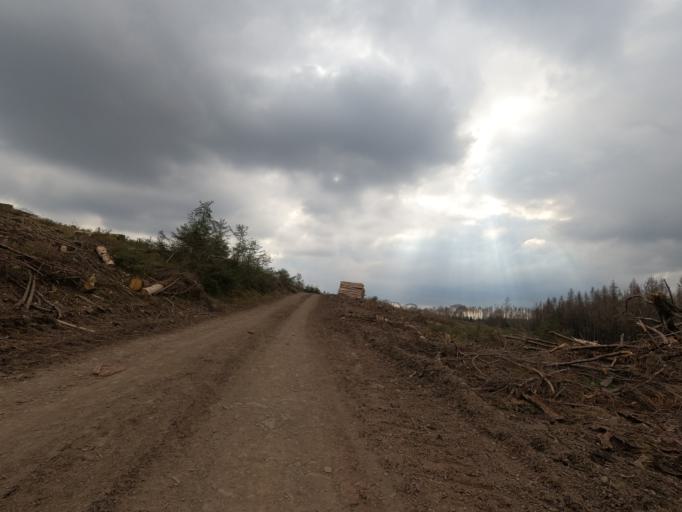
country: DE
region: North Rhine-Westphalia
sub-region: Regierungsbezirk Arnsberg
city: Herscheid
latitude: 51.1632
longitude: 7.7376
